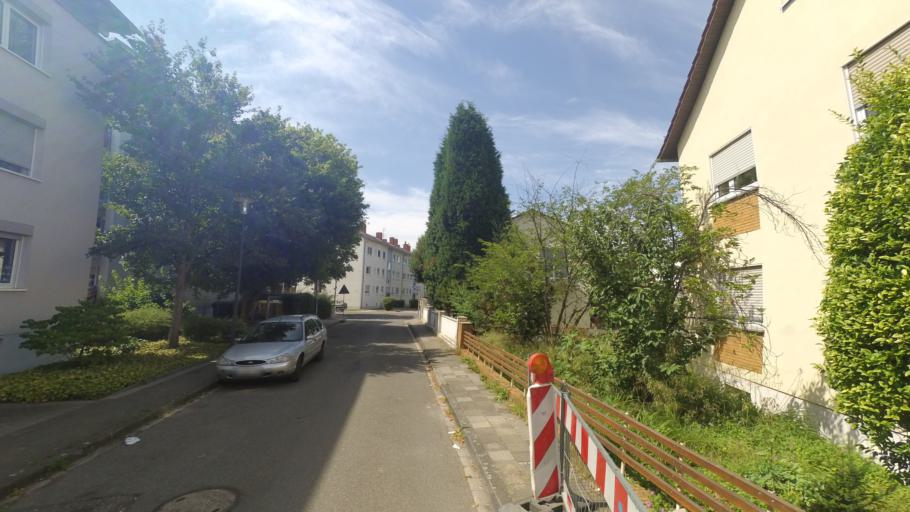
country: DE
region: Rheinland-Pfalz
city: Gartenstadt
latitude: 49.4574
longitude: 8.4231
